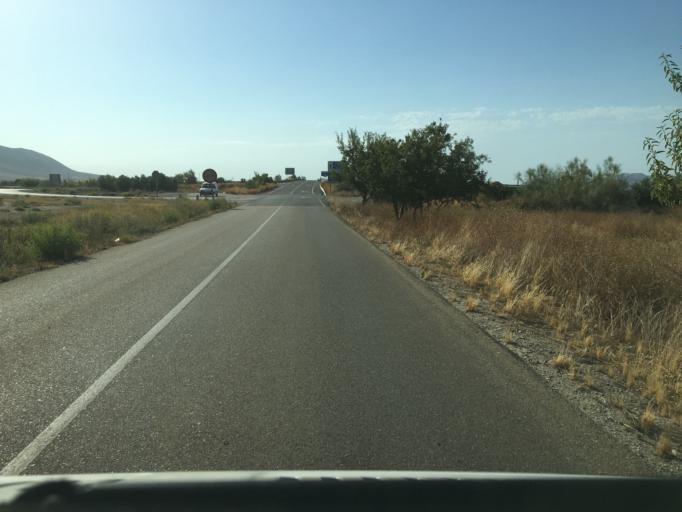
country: ES
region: Andalusia
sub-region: Provincia de Almeria
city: Huercal-Overa
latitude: 37.4666
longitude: -1.8858
